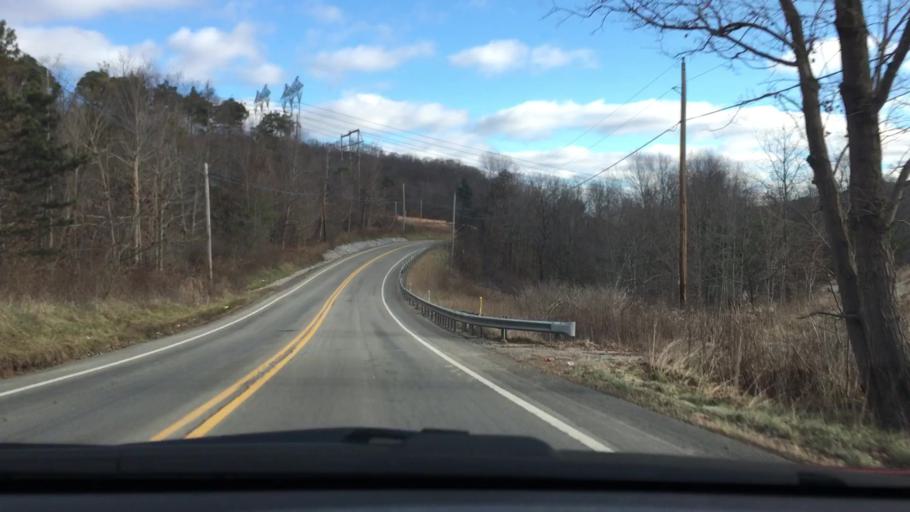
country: US
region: Pennsylvania
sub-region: Westmoreland County
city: Avonmore
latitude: 40.6488
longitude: -79.3296
